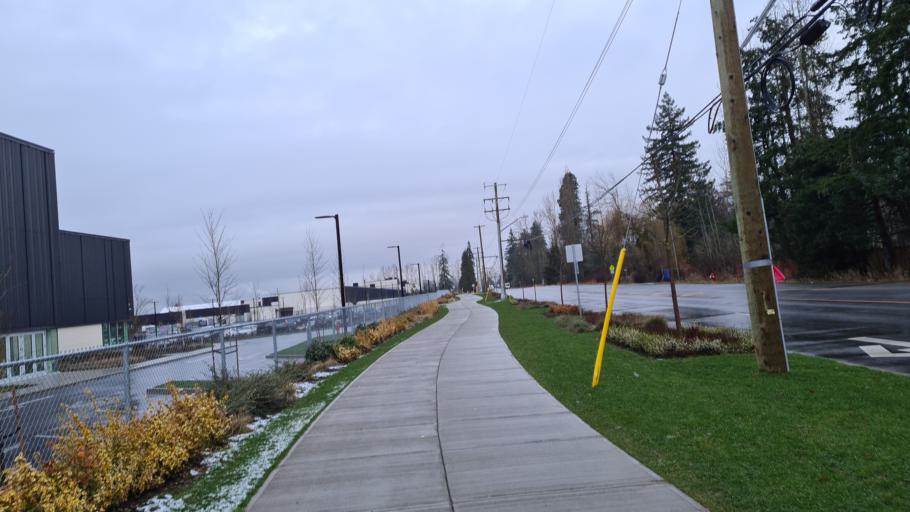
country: CA
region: British Columbia
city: Walnut Grove
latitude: 49.1414
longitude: -122.6617
